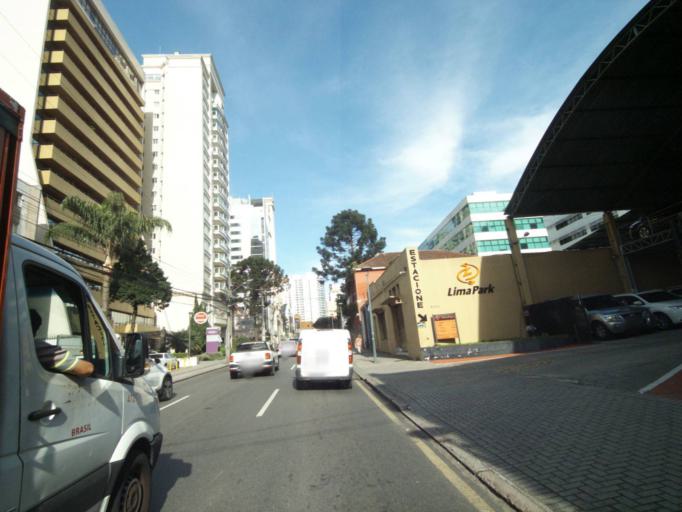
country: BR
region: Parana
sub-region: Curitiba
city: Curitiba
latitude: -25.4366
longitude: -49.2816
